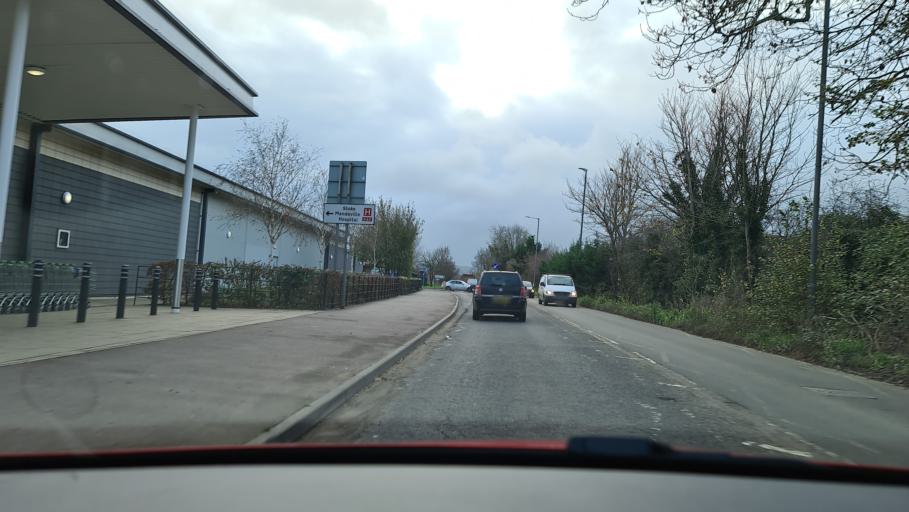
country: GB
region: England
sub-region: Buckinghamshire
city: Aylesbury
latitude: 51.7972
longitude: -0.8052
